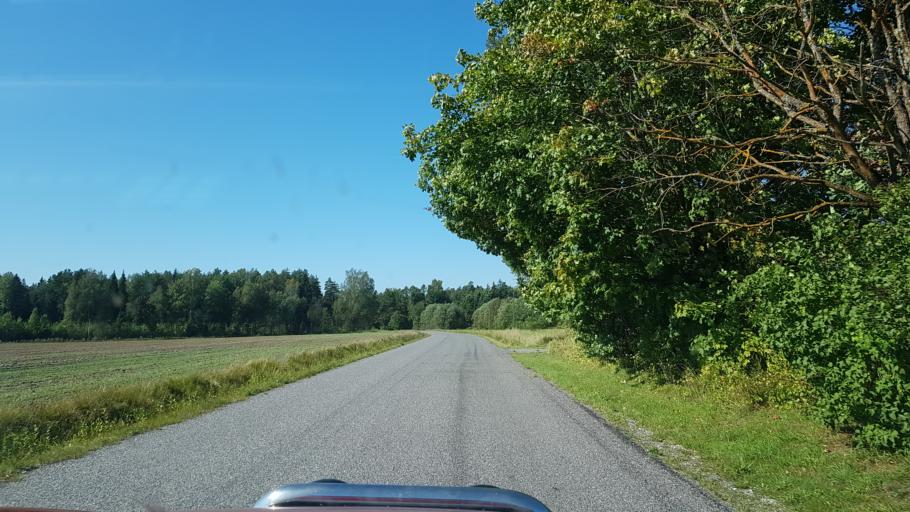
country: EE
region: Polvamaa
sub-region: Polva linn
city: Polva
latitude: 58.2117
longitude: 27.0970
